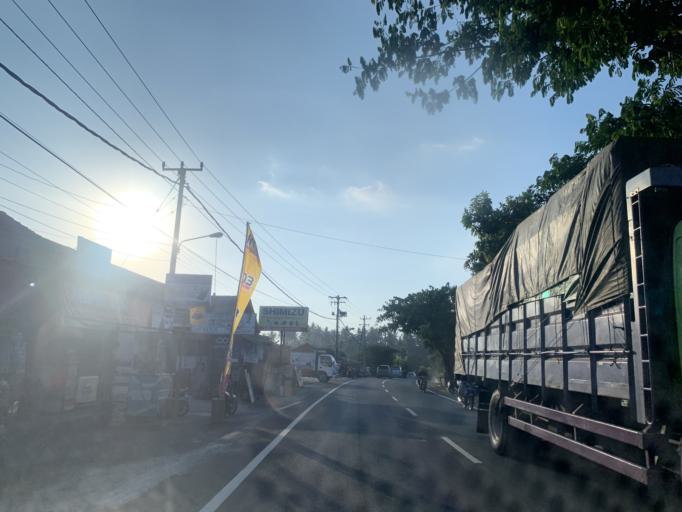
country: ID
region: Bali
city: Banjar Delodrurung
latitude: -8.4945
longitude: 114.9636
